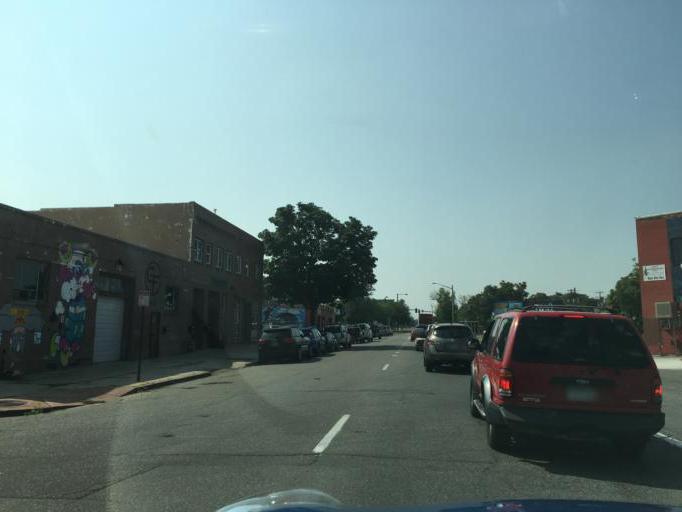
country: US
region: Colorado
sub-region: Denver County
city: Denver
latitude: 39.7682
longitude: -104.9733
